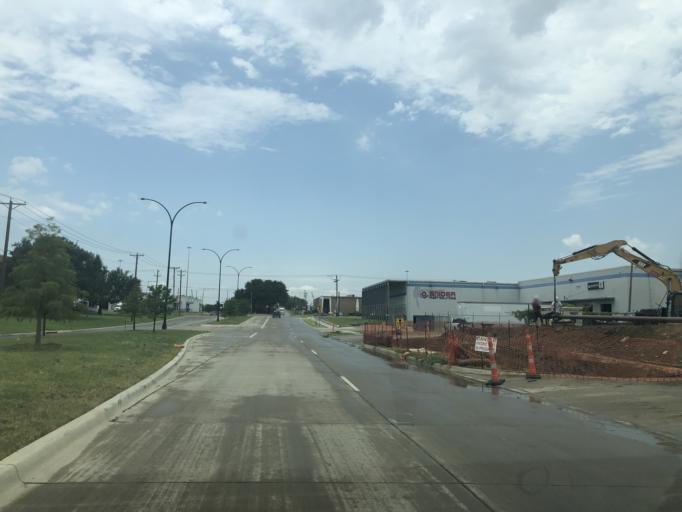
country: US
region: Texas
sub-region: Dallas County
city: Grand Prairie
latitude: 32.7549
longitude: -97.0457
